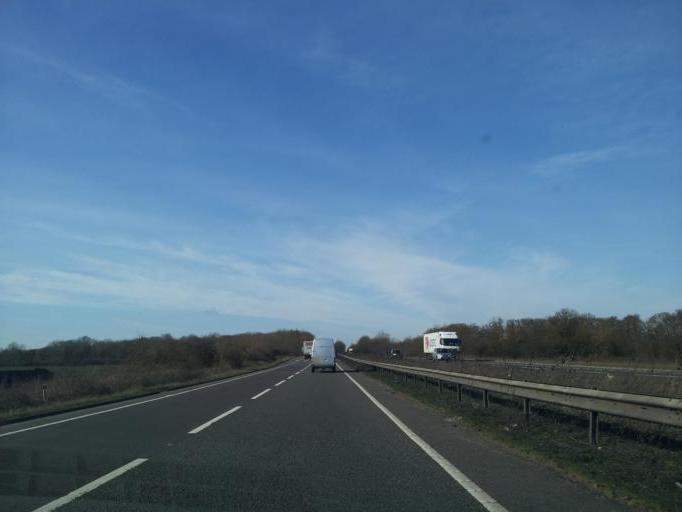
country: GB
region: England
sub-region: District of Rutland
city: Tickencote
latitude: 52.6878
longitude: -0.5560
